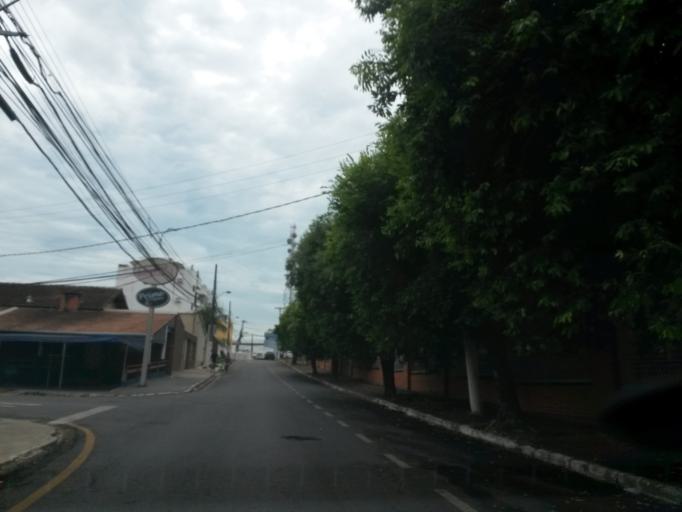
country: BR
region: Mato Grosso
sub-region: Cuiaba
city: Cuiaba
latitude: -15.6051
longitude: -56.0807
